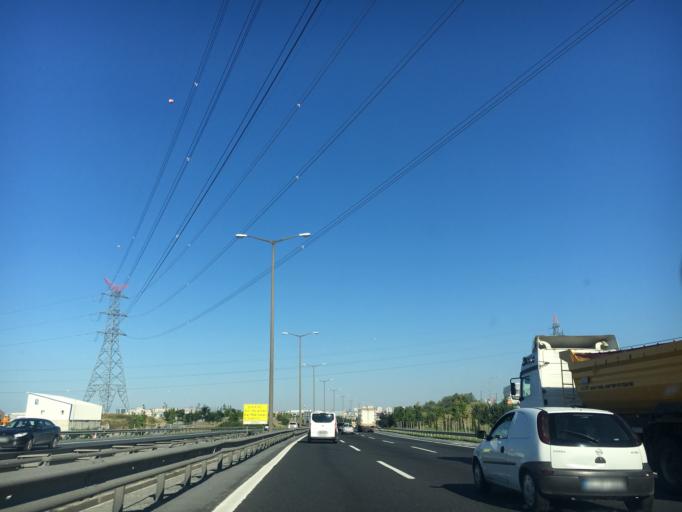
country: TR
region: Istanbul
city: Esenyurt
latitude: 41.0545
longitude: 28.6679
